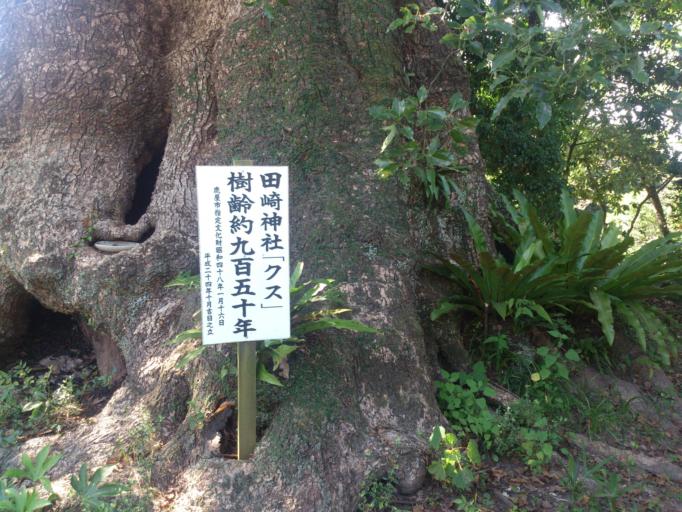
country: JP
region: Kagoshima
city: Kanoya
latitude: 31.3713
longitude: 130.8582
